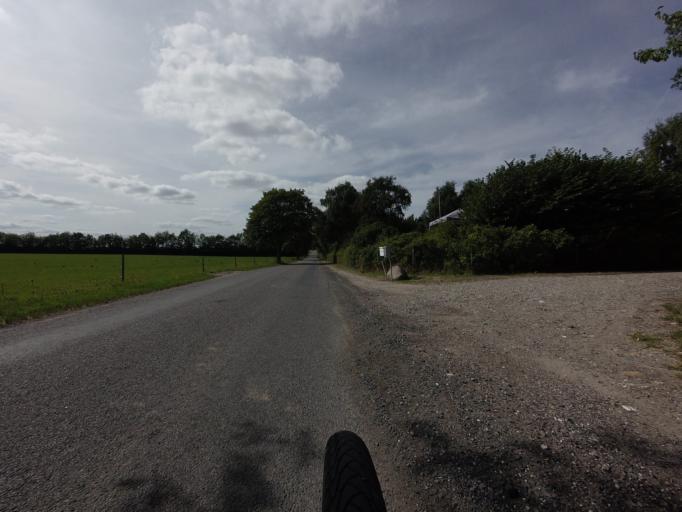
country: DK
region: Zealand
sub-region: Stevns Kommune
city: Store Heddinge
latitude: 55.2451
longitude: 12.2997
